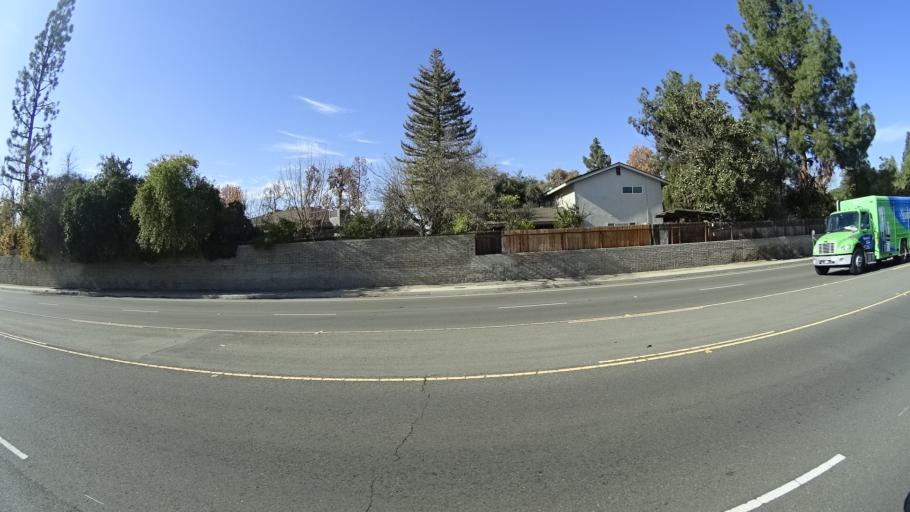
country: US
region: California
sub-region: Kern County
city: Greenacres
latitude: 35.3473
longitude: -119.0747
